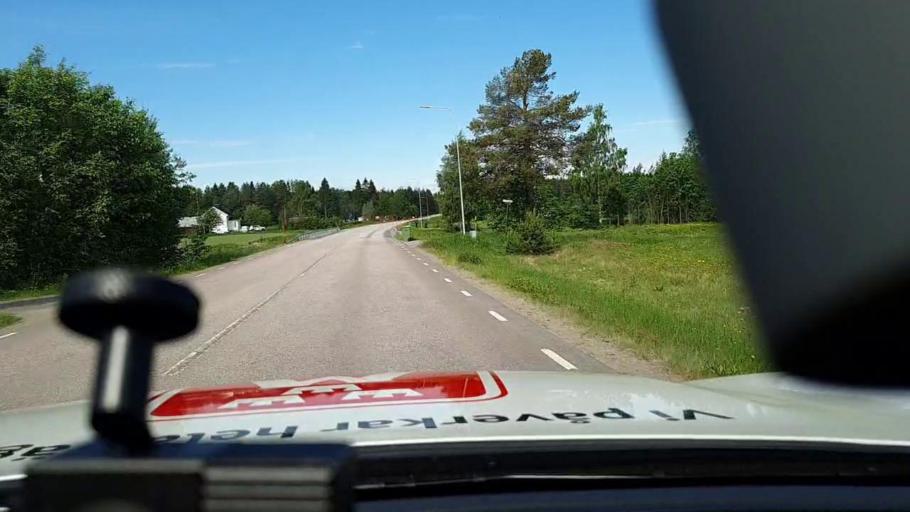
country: SE
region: Norrbotten
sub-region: Lulea Kommun
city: Sodra Sunderbyn
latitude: 65.6429
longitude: 21.8923
